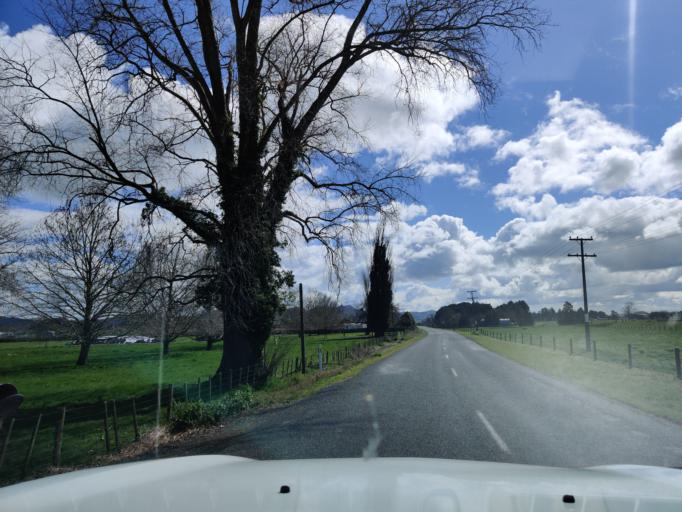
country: NZ
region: Waikato
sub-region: Waikato District
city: Ngaruawahia
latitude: -37.5762
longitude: 175.2689
